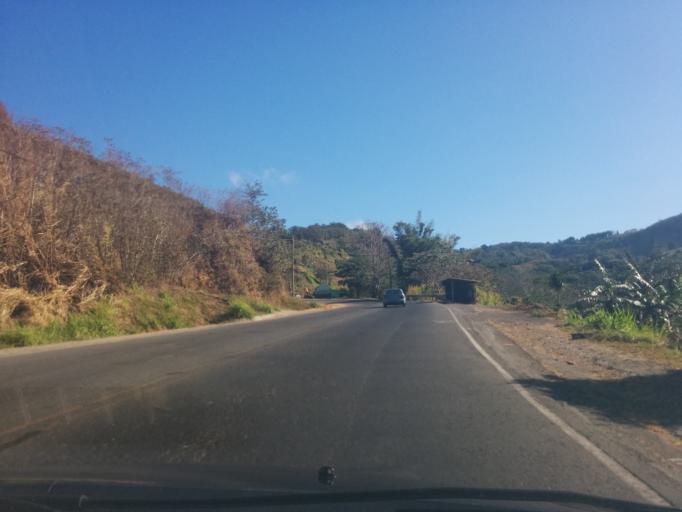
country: CR
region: Alajuela
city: San Rafael
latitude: 10.0375
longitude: -84.5054
